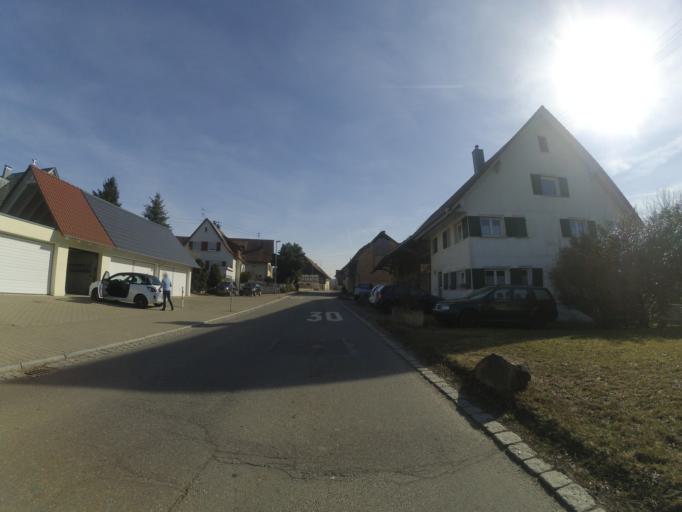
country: DE
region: Baden-Wuerttemberg
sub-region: Tuebingen Region
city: Meckenbeuren
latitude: 47.7339
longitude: 9.5904
